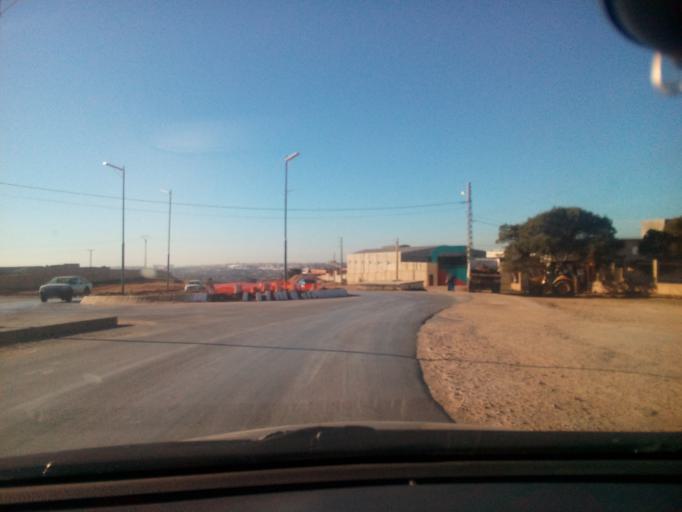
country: DZ
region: Mostaganem
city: Mostaganem
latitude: 35.9123
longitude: 0.1437
